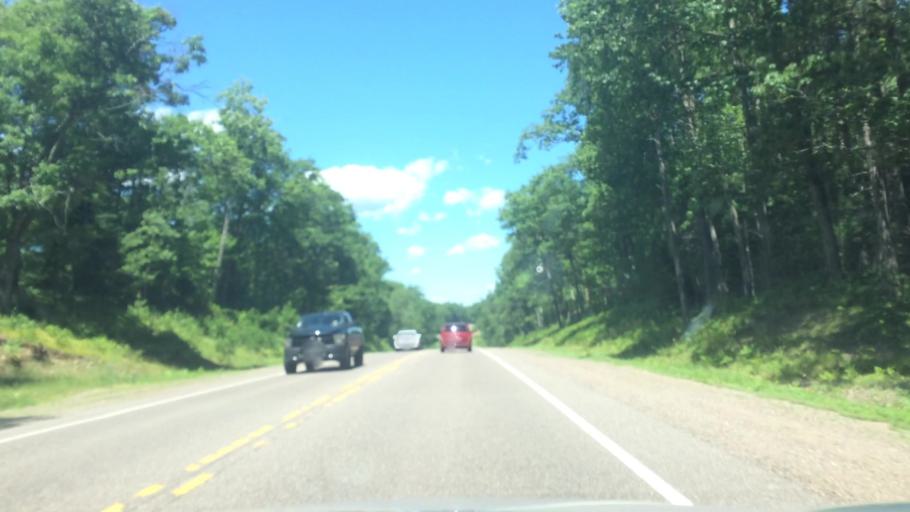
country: US
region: Wisconsin
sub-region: Vilas County
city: Lac du Flambeau
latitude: 45.7733
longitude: -89.7159
